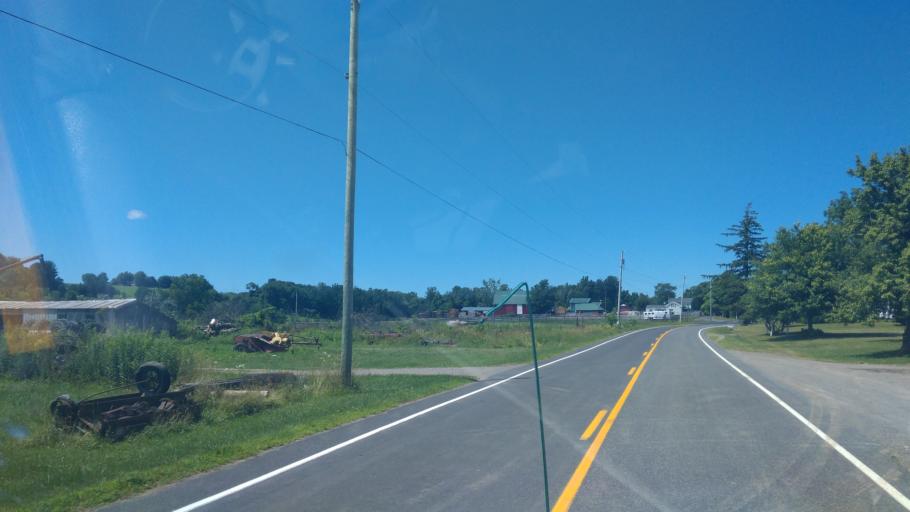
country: US
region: New York
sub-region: Wayne County
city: Lyons
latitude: 43.1340
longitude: -76.9595
